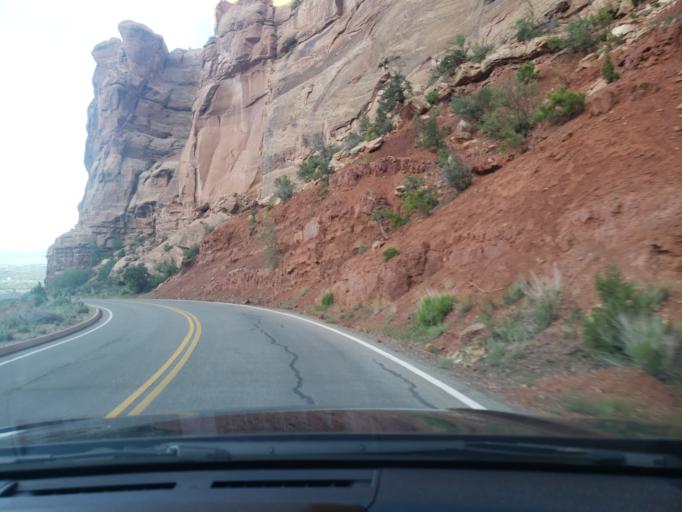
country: US
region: Colorado
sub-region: Mesa County
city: Fruita
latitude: 39.1109
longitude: -108.7316
